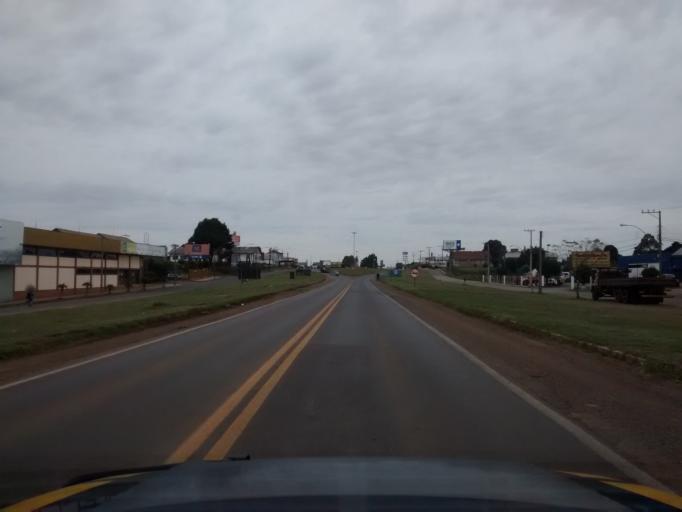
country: BR
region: Rio Grande do Sul
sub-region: Vacaria
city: Vacaria
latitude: -28.5029
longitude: -50.9223
